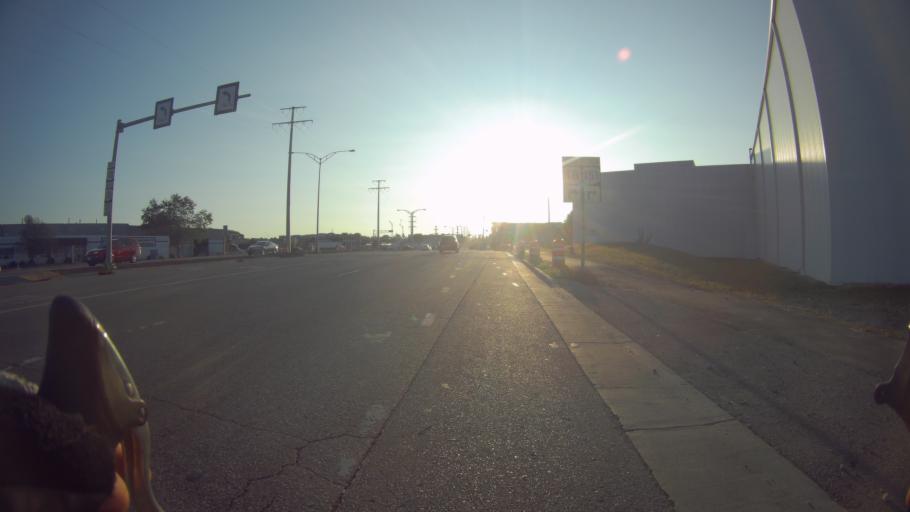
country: US
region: Wisconsin
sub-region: Dane County
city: Fitchburg
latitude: 43.0157
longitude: -89.4709
